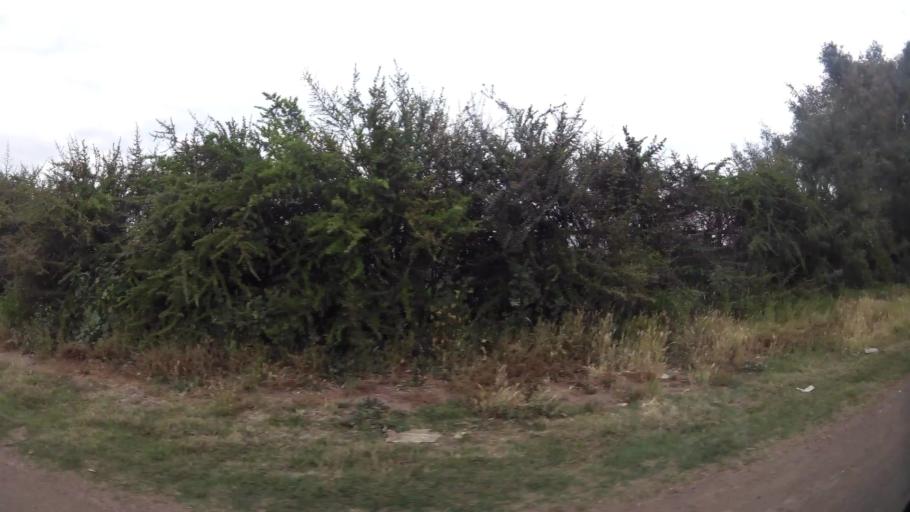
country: CL
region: Santiago Metropolitan
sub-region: Provincia de Chacabuco
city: Chicureo Abajo
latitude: -33.2271
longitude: -70.6732
